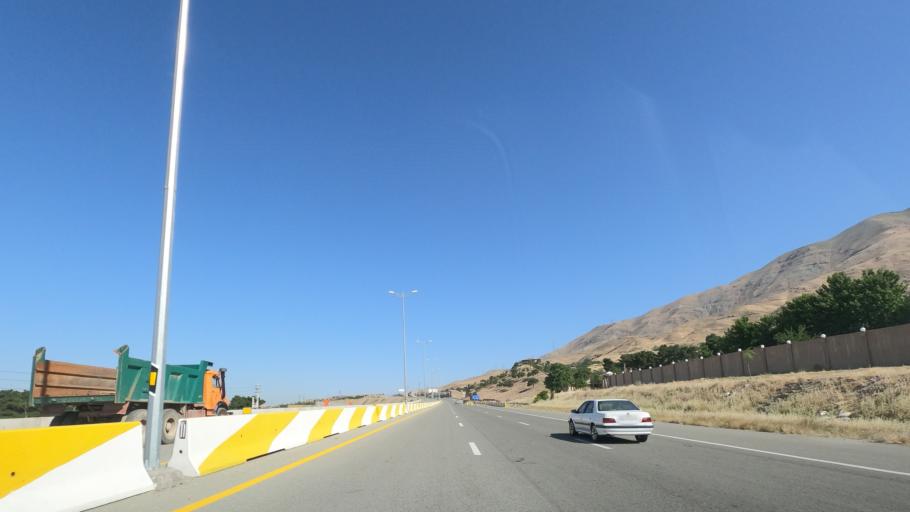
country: IR
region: Tehran
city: Shahr-e Qods
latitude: 35.7583
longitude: 51.0778
